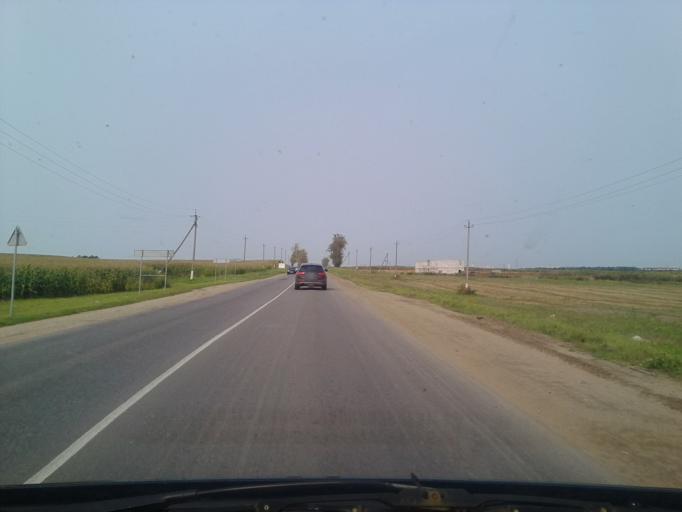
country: BY
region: Minsk
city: Hatava
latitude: 53.7849
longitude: 27.6537
